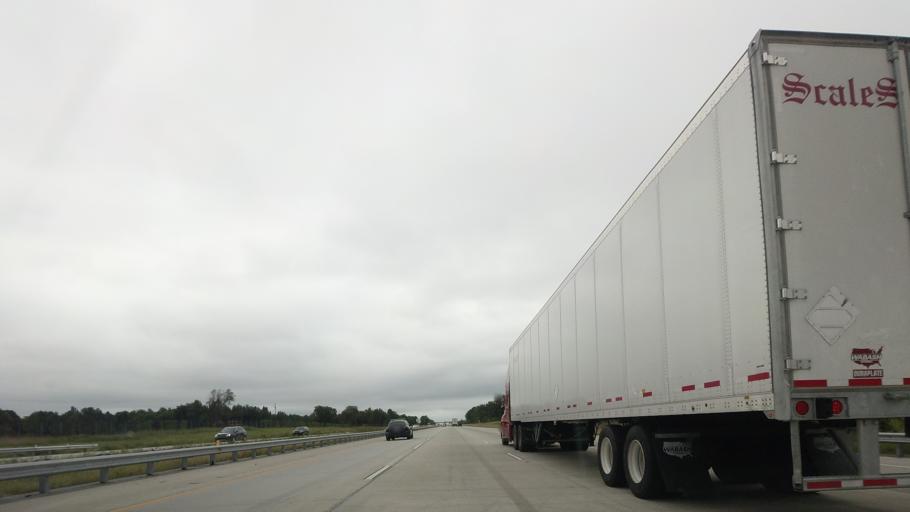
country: US
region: Georgia
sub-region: Dooly County
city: Unadilla
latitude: 32.1865
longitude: -83.7491
